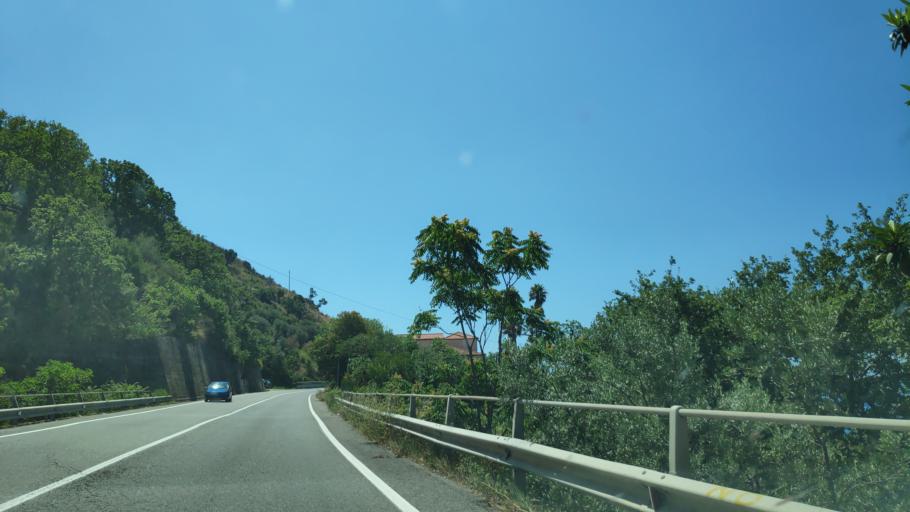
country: IT
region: Calabria
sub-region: Provincia di Cosenza
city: Cittadella del Capo
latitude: 39.5545
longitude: 15.8805
